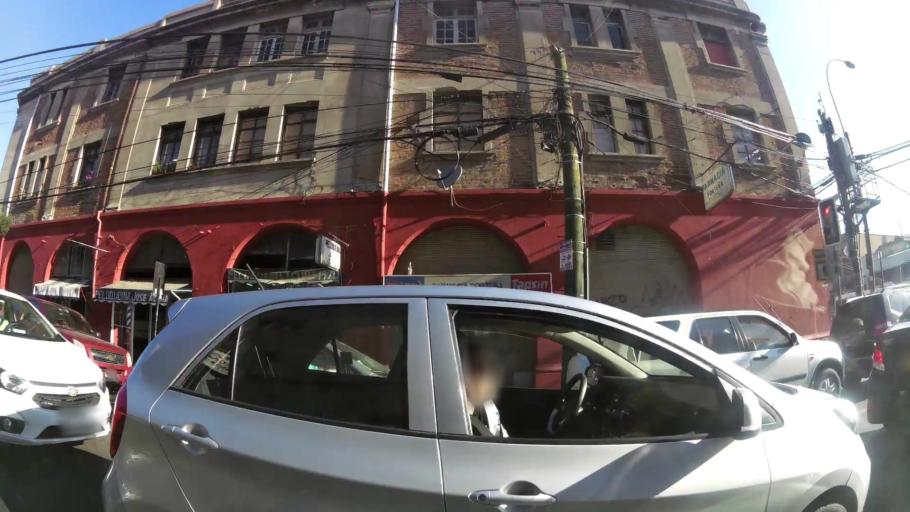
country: CL
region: Valparaiso
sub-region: Provincia de Valparaiso
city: Valparaiso
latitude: -33.0459
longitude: -71.6042
